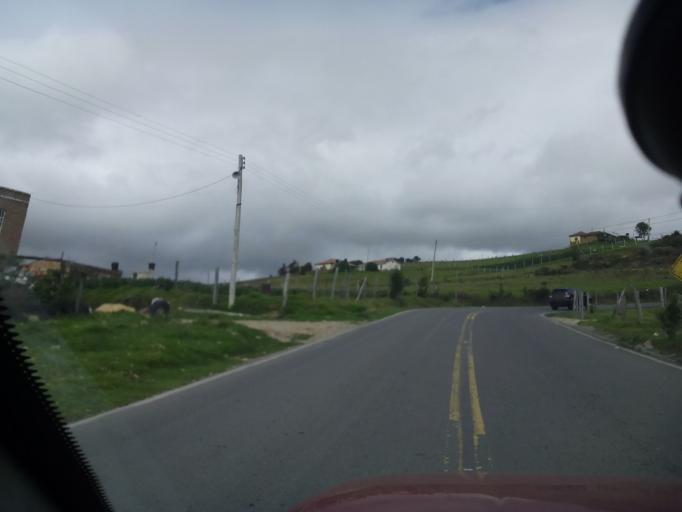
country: CO
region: Boyaca
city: Combita
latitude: 5.6296
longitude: -73.3370
